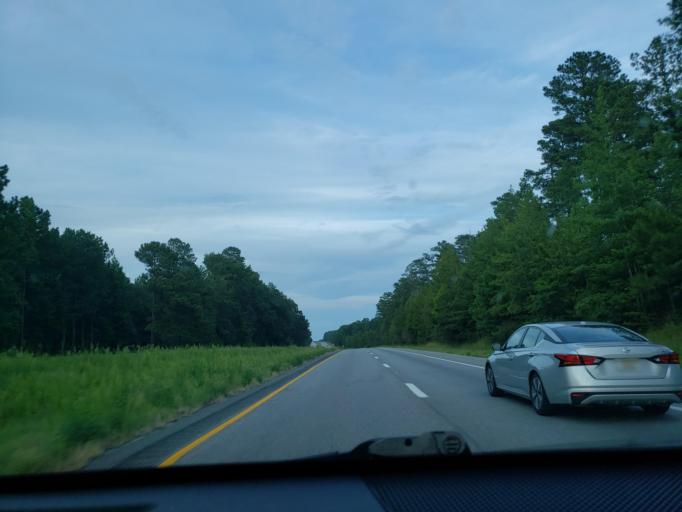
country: US
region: Virginia
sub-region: City of Emporia
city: Emporia
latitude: 36.6913
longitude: -77.3554
